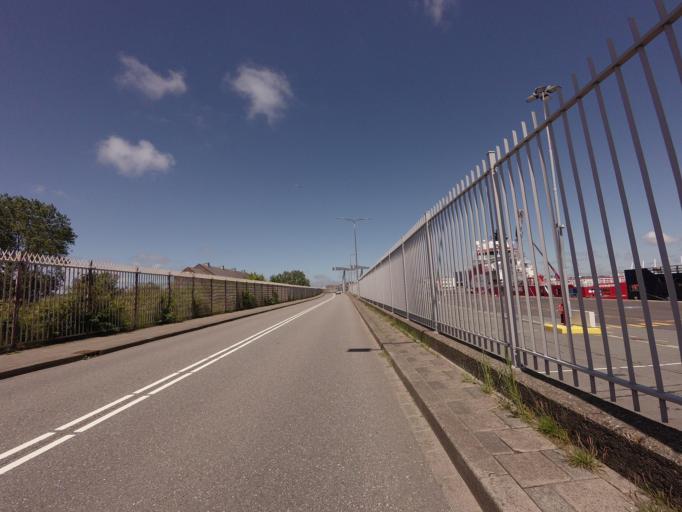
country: NL
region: North Holland
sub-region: Gemeente Den Helder
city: Den Helder
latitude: 52.9588
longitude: 4.7754
